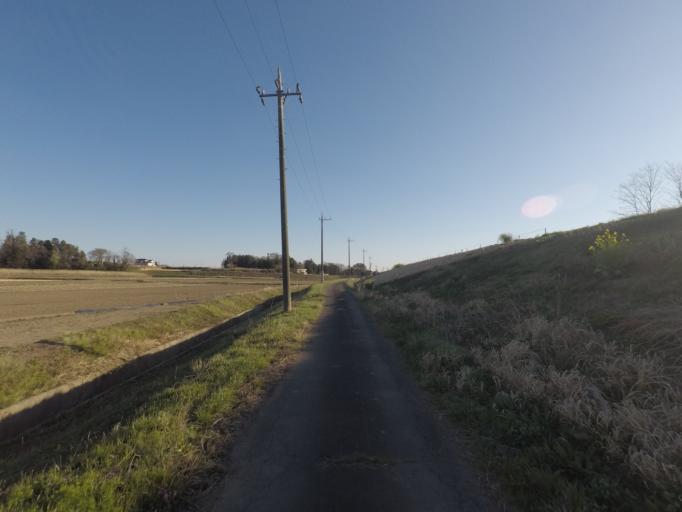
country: JP
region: Ibaraki
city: Ishige
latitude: 36.1631
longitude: 140.0077
